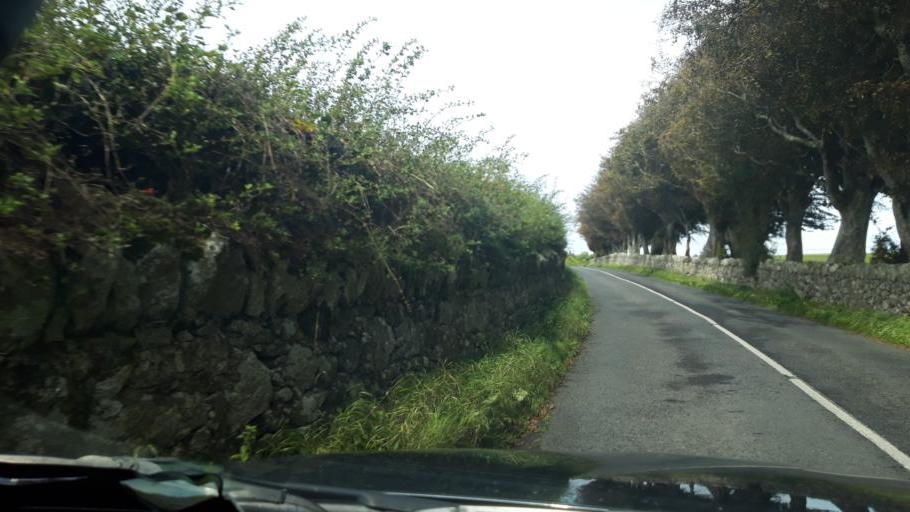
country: IE
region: Leinster
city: Sandyford
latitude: 53.2262
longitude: -6.2205
